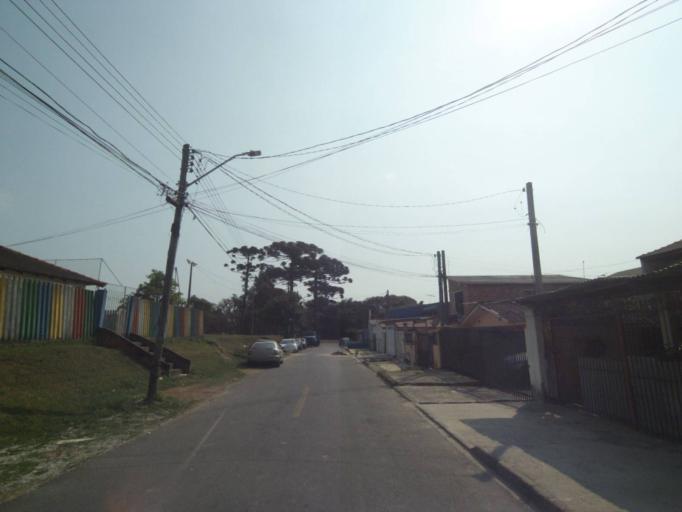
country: BR
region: Parana
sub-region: Pinhais
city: Pinhais
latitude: -25.4827
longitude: -49.2034
